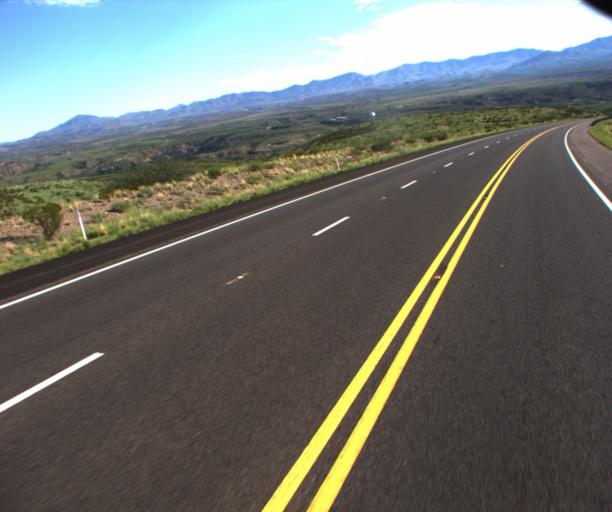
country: US
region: Arizona
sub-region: Greenlee County
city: Clifton
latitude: 32.9240
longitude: -109.2445
